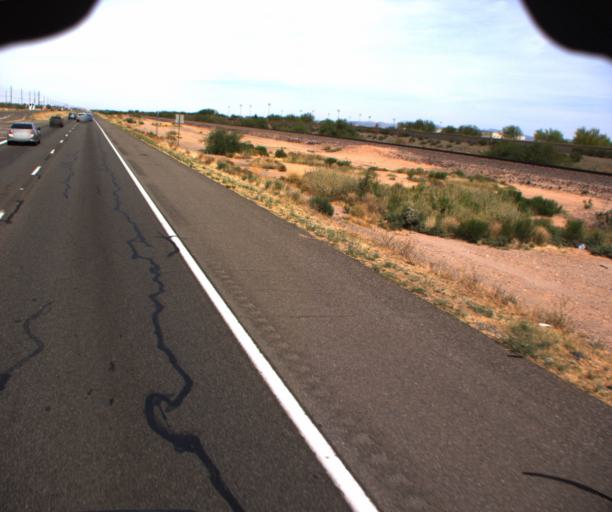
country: US
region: Arizona
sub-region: Maricopa County
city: Sun City West
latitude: 33.6908
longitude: -112.4169
